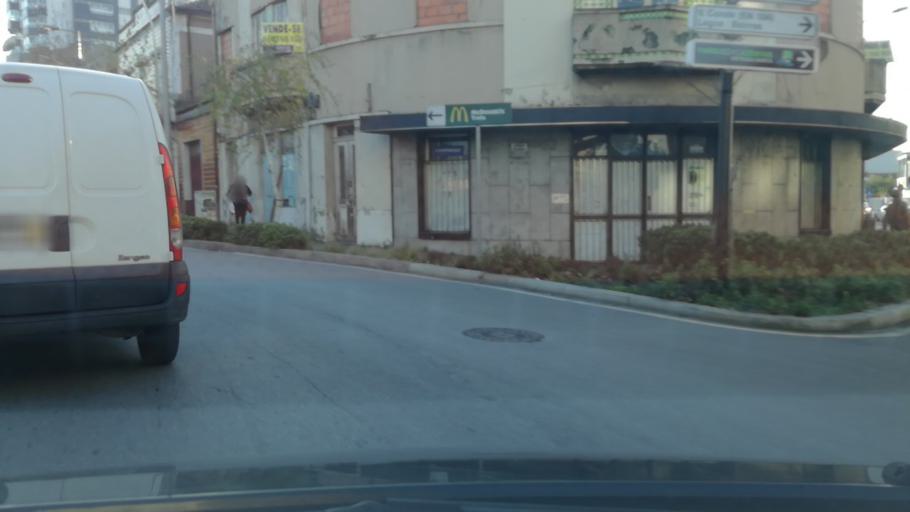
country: PT
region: Porto
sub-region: Trofa
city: Bougado
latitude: 41.3374
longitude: -8.5597
